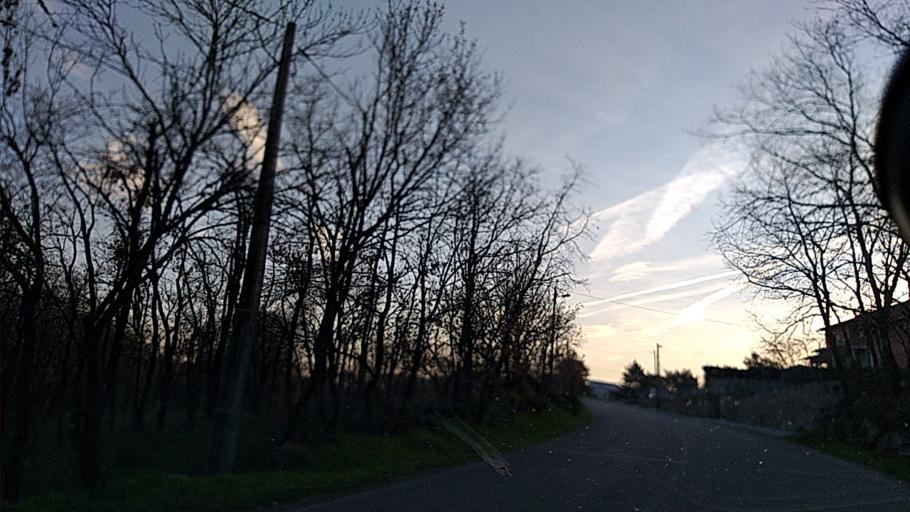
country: PT
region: Guarda
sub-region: Pinhel
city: Pinhel
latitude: 40.6018
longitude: -7.0576
